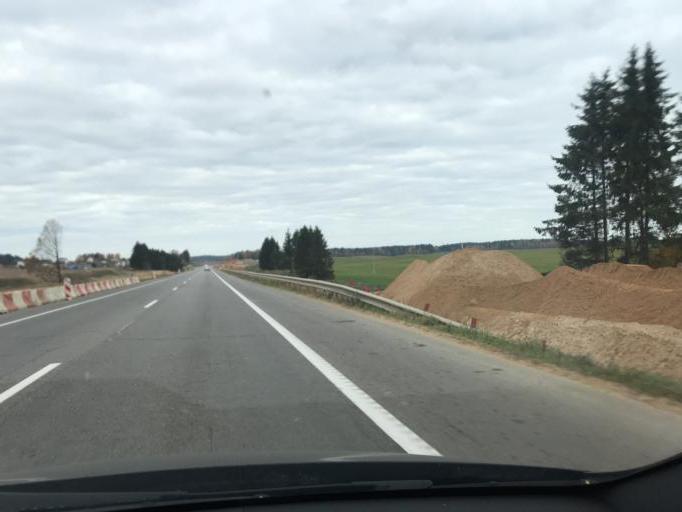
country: BY
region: Minsk
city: Slabada
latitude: 54.0265
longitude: 27.8782
